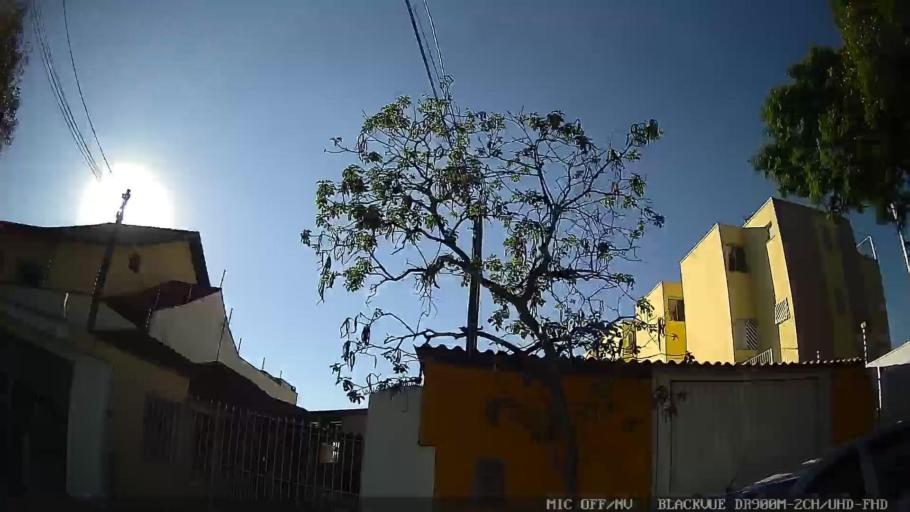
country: BR
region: Sao Paulo
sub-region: Guarulhos
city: Guarulhos
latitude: -23.5316
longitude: -46.5069
